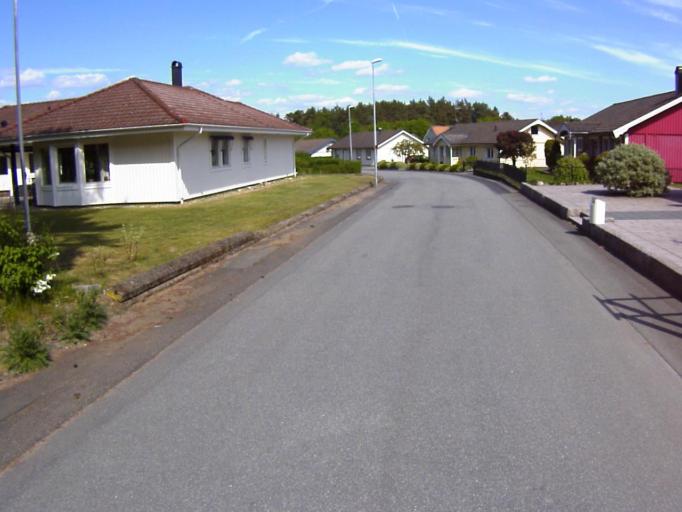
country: SE
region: Skane
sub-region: Ostra Goinge Kommun
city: Hanaskog
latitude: 56.0784
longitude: 14.0912
